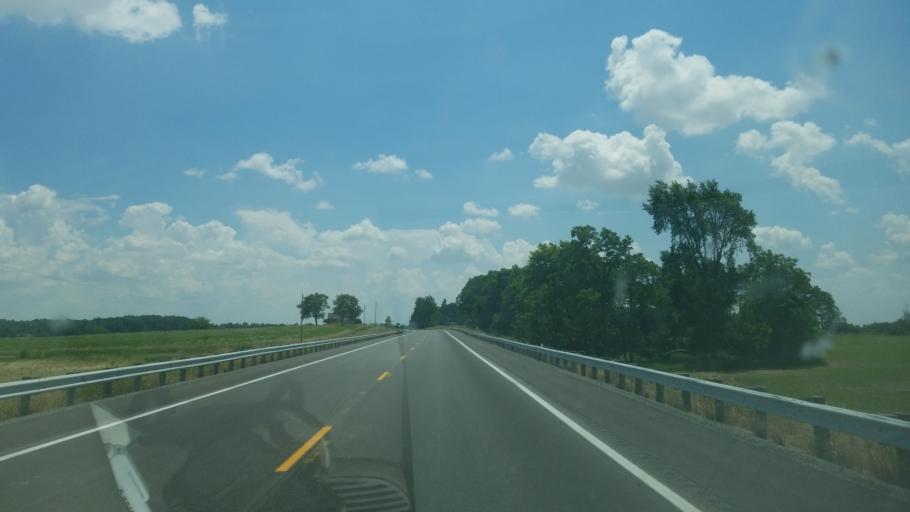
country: US
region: Ohio
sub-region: Hardin County
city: Ada
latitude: 40.7125
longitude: -83.7552
